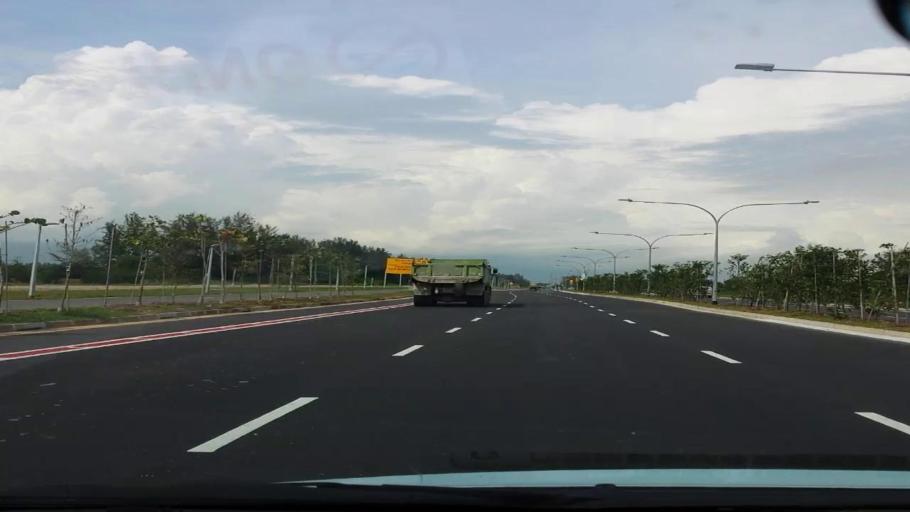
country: SG
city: Singapore
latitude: 1.3414
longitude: 104.0255
